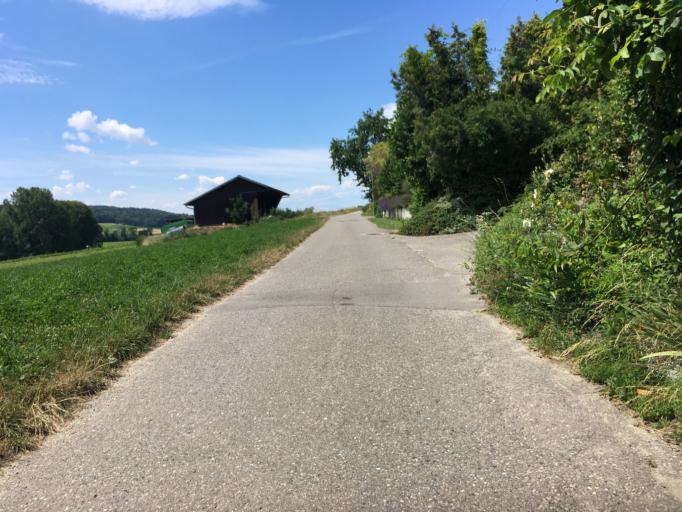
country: CH
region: Neuchatel
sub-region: Neuchatel District
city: Saint-Blaise
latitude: 46.9500
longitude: 7.0163
